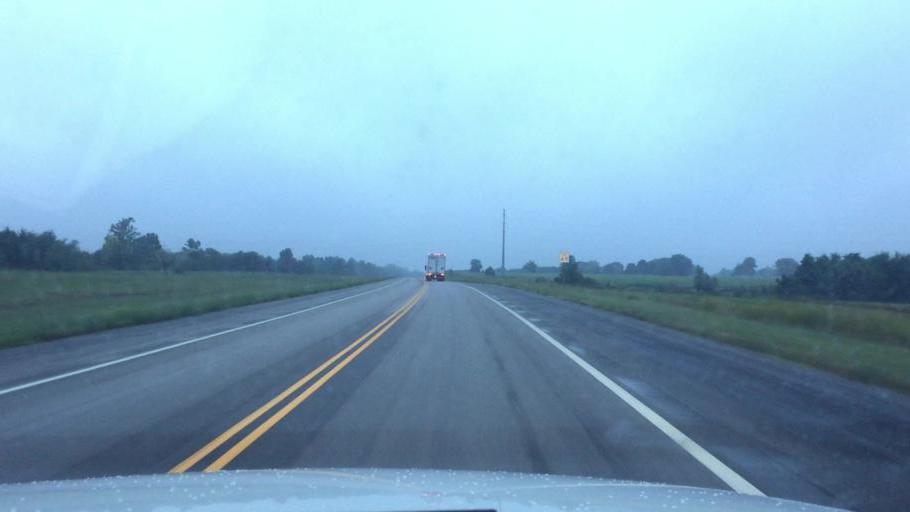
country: US
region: Kansas
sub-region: Montgomery County
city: Cherryvale
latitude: 37.4545
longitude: -95.4826
